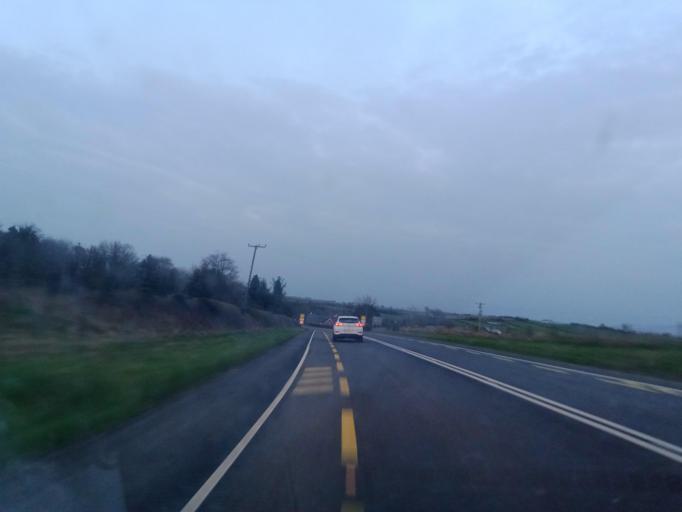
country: IE
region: Leinster
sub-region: Laois
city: Abbeyleix
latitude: 52.8590
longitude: -7.3732
